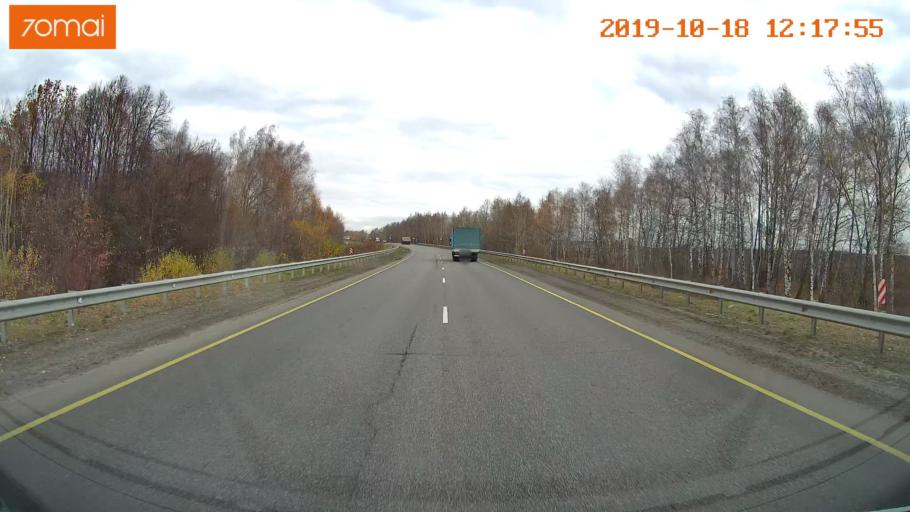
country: RU
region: Rjazan
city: Zakharovo
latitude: 54.4614
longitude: 39.4515
